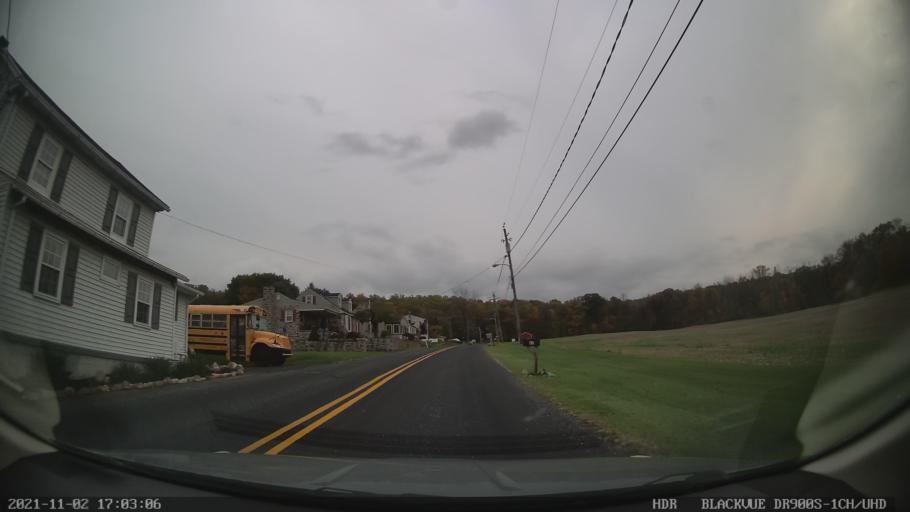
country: US
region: Pennsylvania
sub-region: Berks County
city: Fleetwood
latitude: 40.4455
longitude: -75.8416
